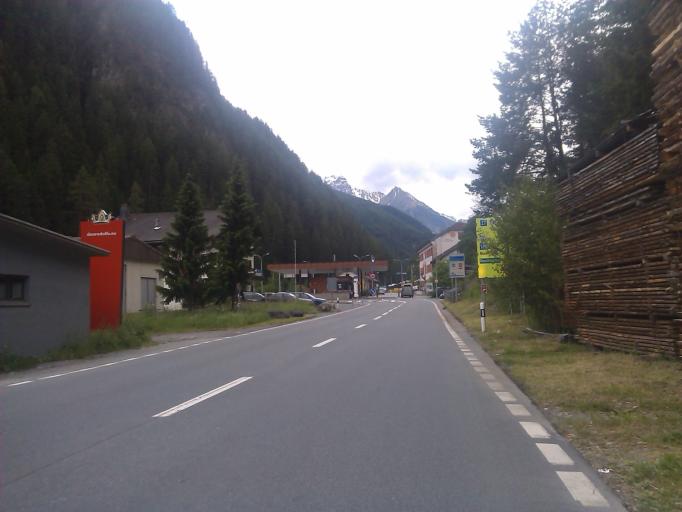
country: AT
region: Tyrol
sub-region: Politischer Bezirk Landeck
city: Nauders
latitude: 46.8861
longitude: 10.4652
